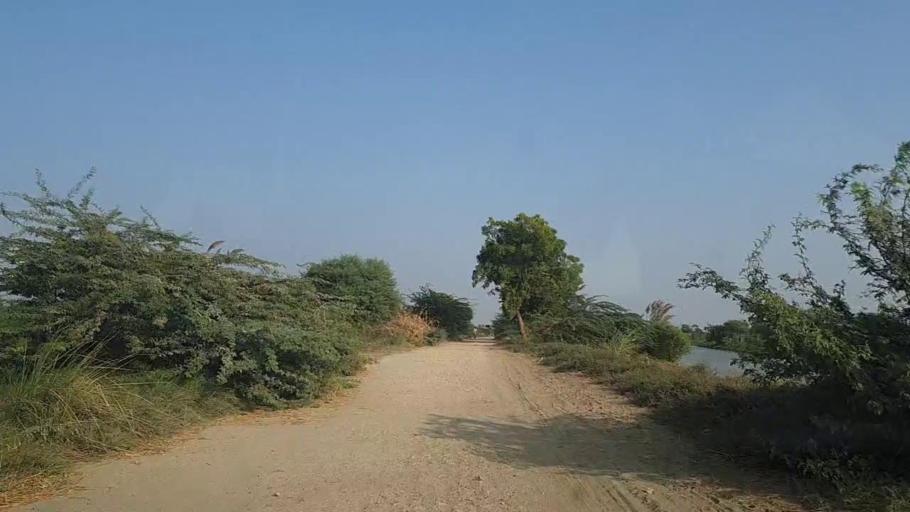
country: PK
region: Sindh
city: Mirpur Sakro
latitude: 24.5756
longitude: 67.6732
